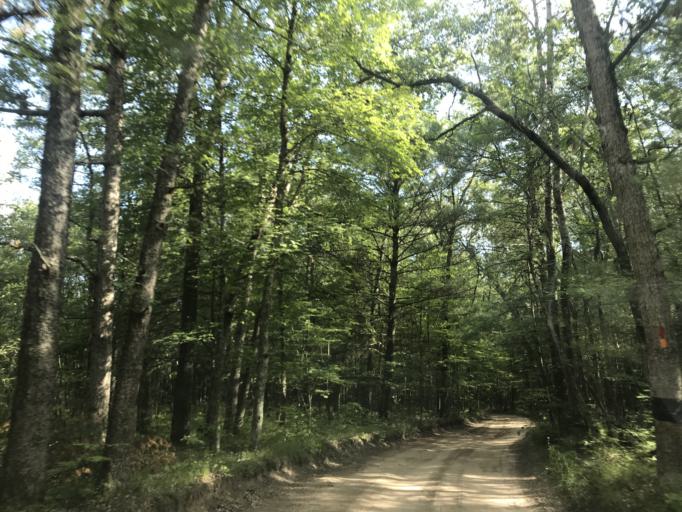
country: US
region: Michigan
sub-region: Newaygo County
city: Newaygo
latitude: 43.4566
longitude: -85.7617
